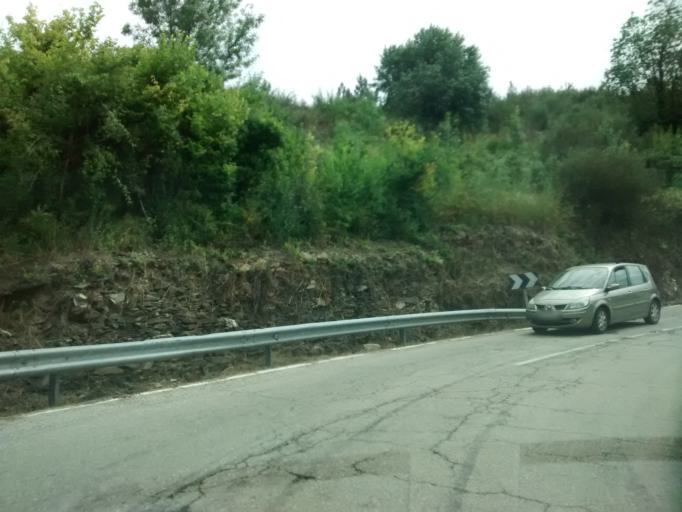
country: ES
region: Galicia
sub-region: Provincia de Ourense
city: Petin
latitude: 42.3454
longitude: -7.1757
